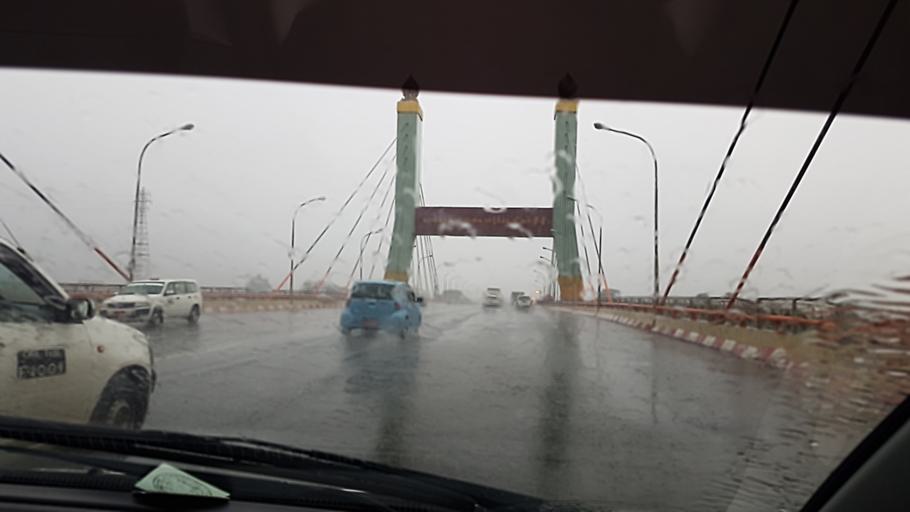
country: MM
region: Yangon
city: Yangon
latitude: 16.7765
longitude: 96.1831
